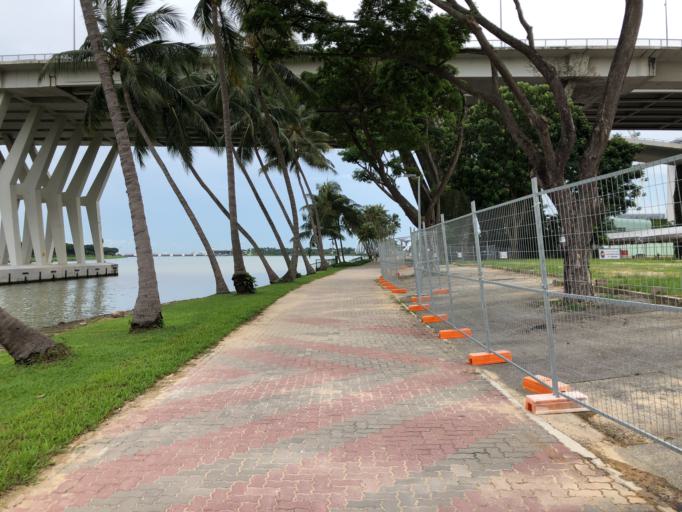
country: SG
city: Singapore
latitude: 1.2949
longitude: 103.8642
